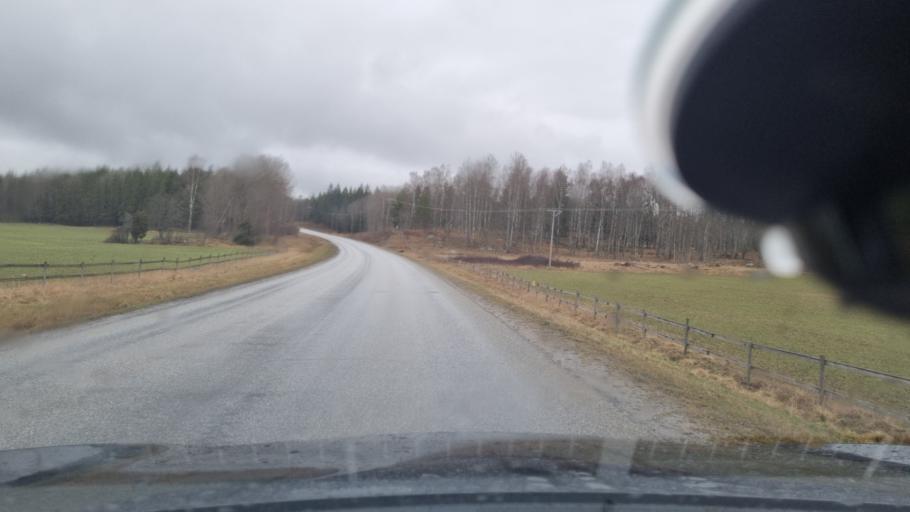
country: SE
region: Stockholm
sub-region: Sigtuna Kommun
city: Sigtuna
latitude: 59.5504
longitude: 17.7352
